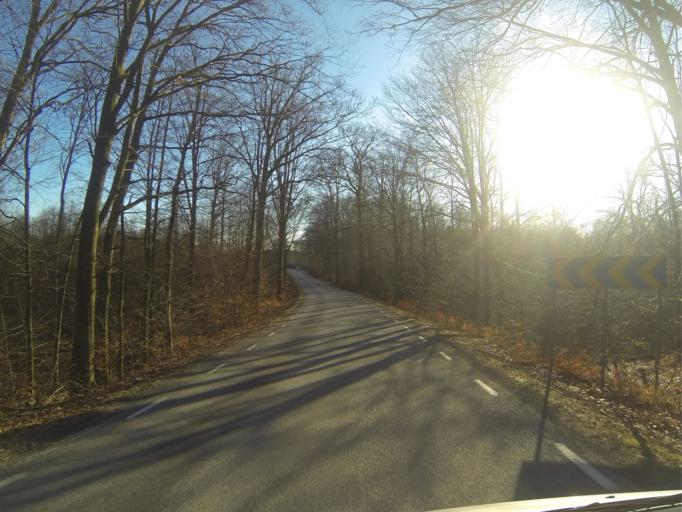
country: SE
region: Skane
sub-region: Horby Kommun
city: Hoerby
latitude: 55.9070
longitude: 13.6580
